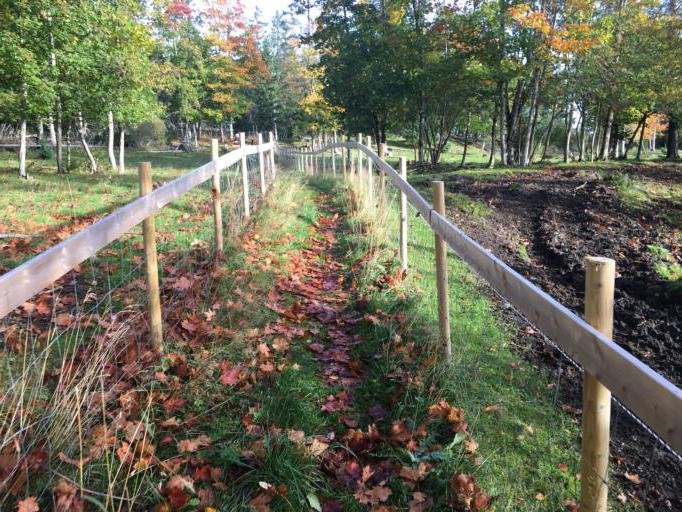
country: NO
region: Nord-Trondelag
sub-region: Leksvik
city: Leksvik
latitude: 63.5722
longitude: 10.6124
